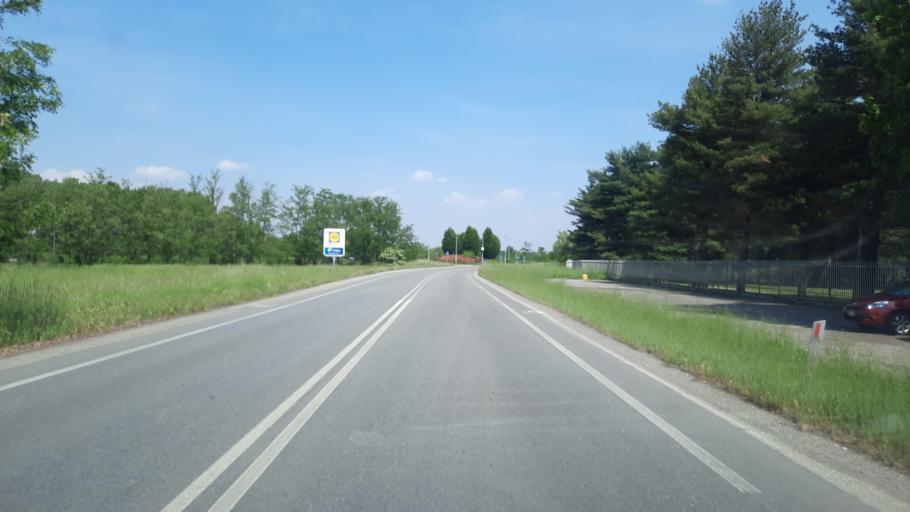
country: IT
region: Lombardy
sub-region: Provincia di Pavia
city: Garlasco
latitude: 45.1912
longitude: 8.9357
